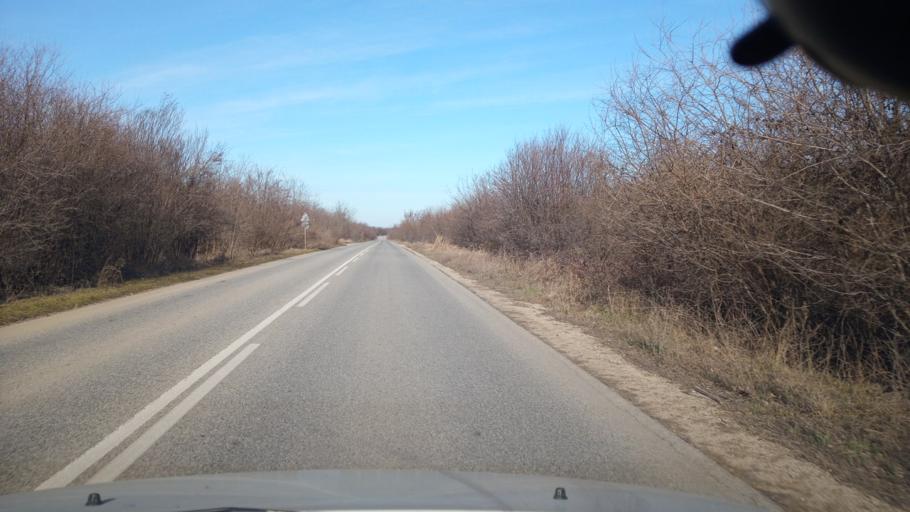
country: BG
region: Pleven
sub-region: Obshtina Pleven
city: Pleven
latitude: 43.4316
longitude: 24.7201
